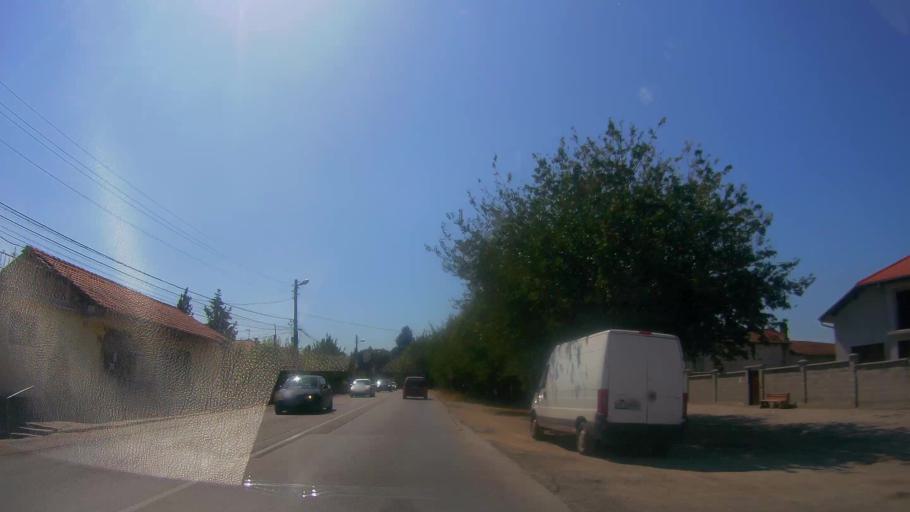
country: BG
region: Veliko Turnovo
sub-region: Obshtina Gorna Oryakhovitsa
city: Purvomaytsi
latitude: 43.1827
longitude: 25.6196
